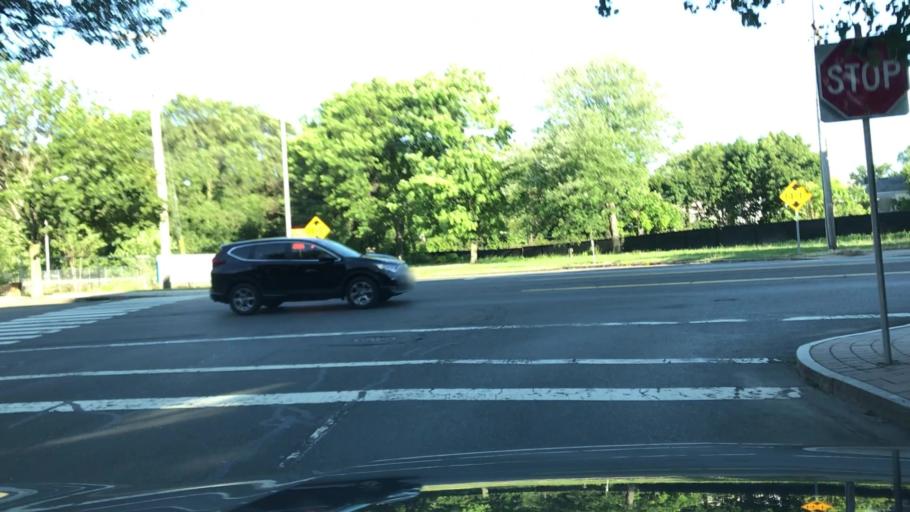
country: US
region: Connecticut
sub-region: New Haven County
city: New Haven
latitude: 41.3108
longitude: -72.9176
